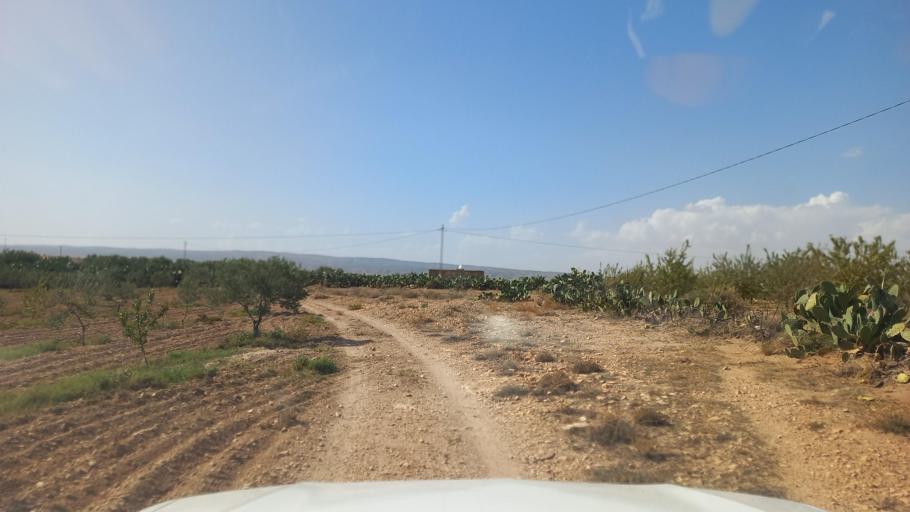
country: TN
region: Al Qasrayn
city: Kasserine
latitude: 35.2727
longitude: 9.0267
